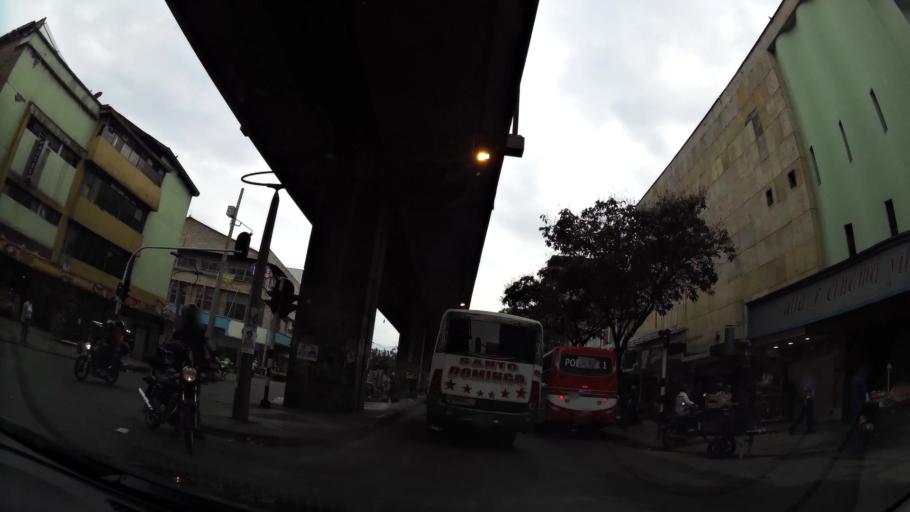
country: CO
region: Antioquia
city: Medellin
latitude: 6.2538
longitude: -75.5674
